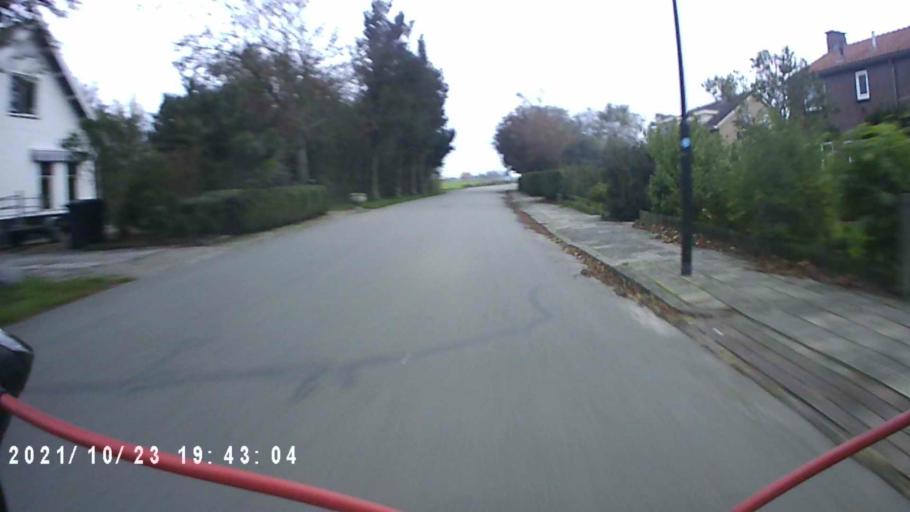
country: NL
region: Friesland
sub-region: Sudwest Fryslan
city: Makkum
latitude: 53.0830
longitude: 5.4250
